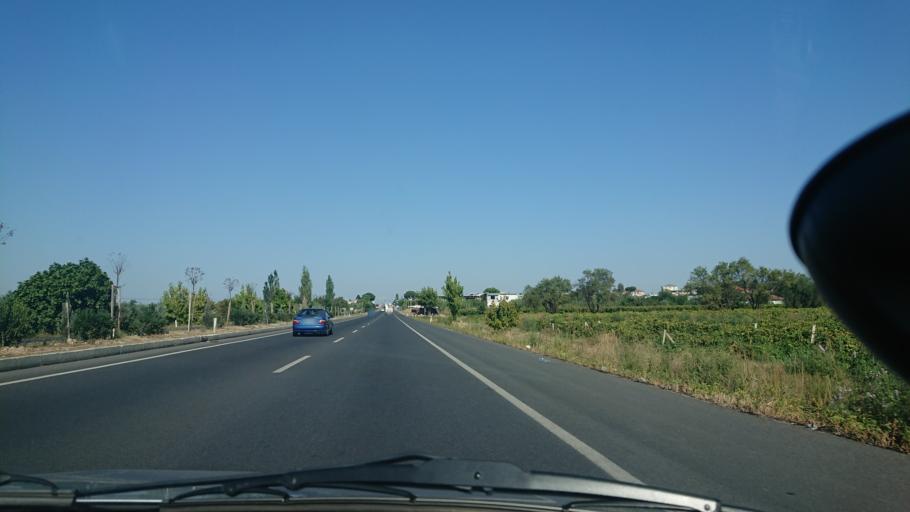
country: TR
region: Manisa
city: Ahmetli
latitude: 38.4980
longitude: 27.8639
